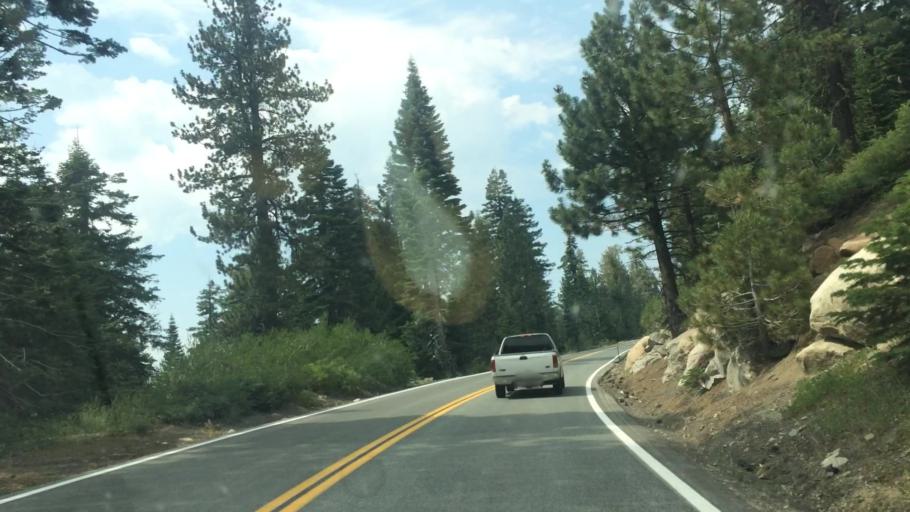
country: US
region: California
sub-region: El Dorado County
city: South Lake Tahoe
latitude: 38.6866
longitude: -120.1228
